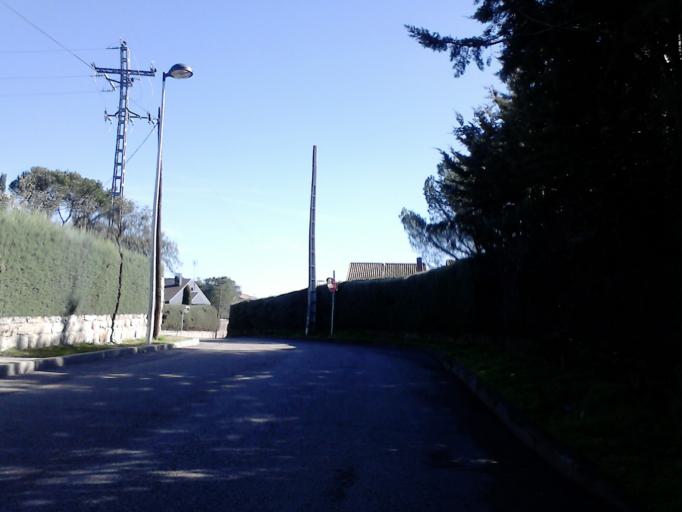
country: ES
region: Madrid
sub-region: Provincia de Madrid
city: Galapagar
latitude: 40.5692
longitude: -3.9967
